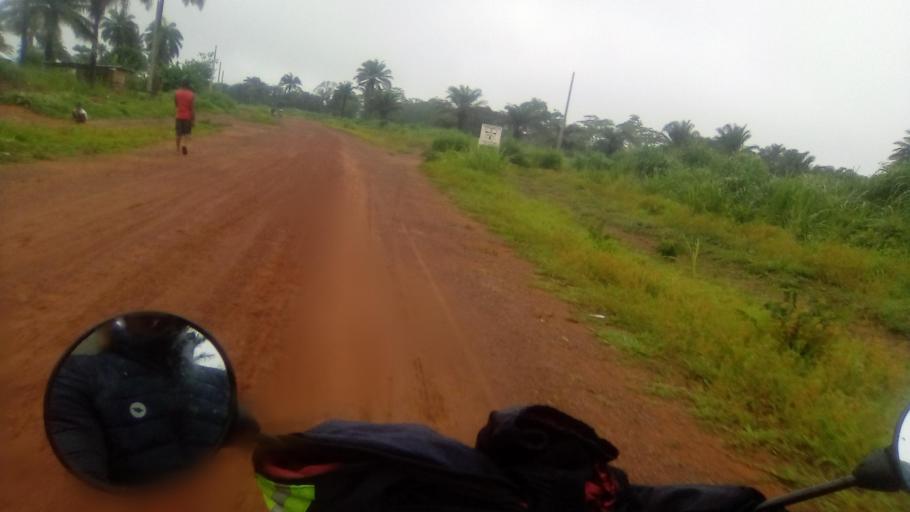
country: SL
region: Southern Province
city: Moyamba
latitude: 8.1469
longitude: -12.4381
